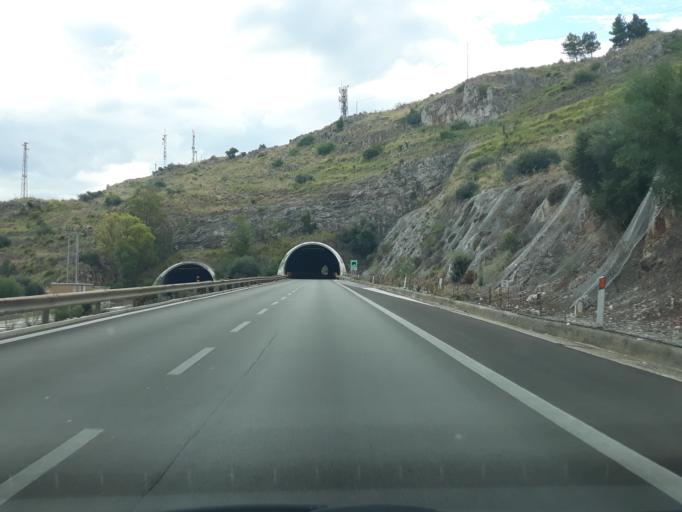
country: IT
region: Sicily
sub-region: Palermo
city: Trabia
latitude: 37.9949
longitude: 13.6489
